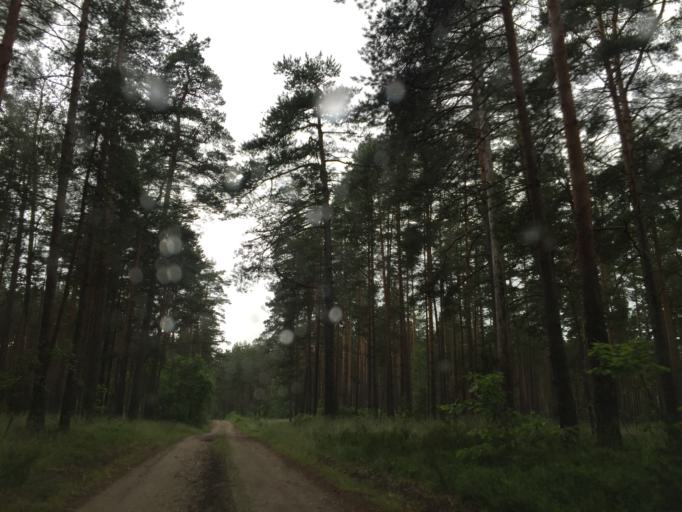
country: LV
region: Riga
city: Jaunciems
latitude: 57.0595
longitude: 24.1926
